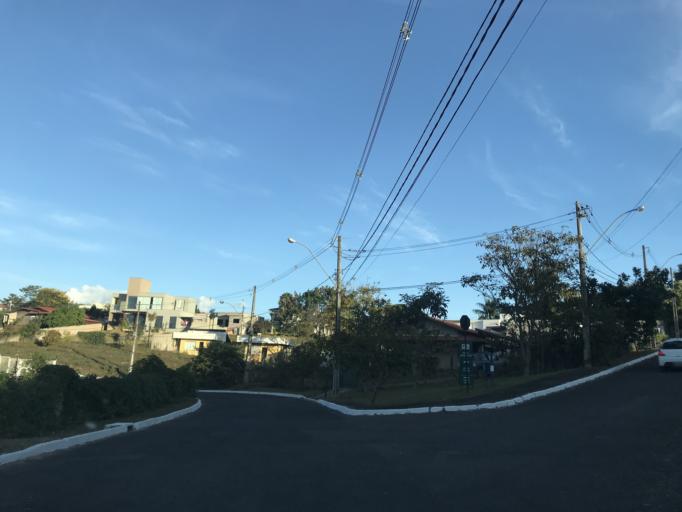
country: BR
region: Federal District
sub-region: Brasilia
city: Brasilia
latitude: -15.8839
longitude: -47.7630
